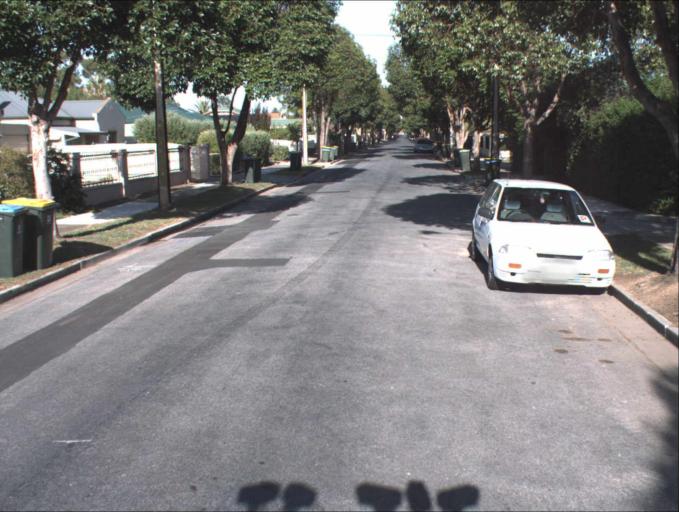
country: AU
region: South Australia
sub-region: Prospect
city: Prospect
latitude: -34.8872
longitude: 138.5826
